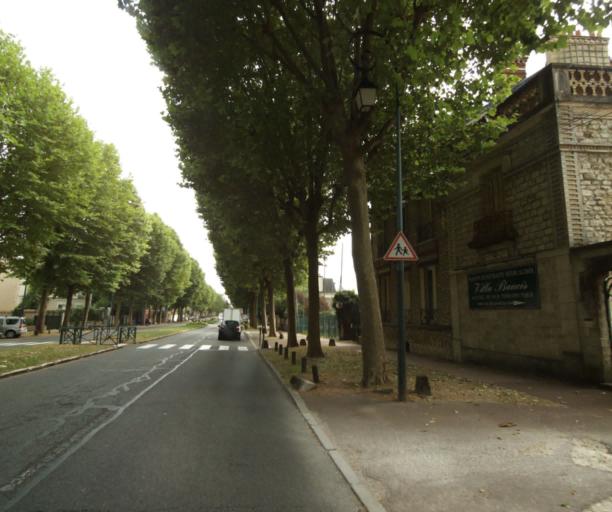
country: FR
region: Ile-de-France
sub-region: Departement de Seine-et-Marne
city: Fontainebleau
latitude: 48.4165
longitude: 2.7071
